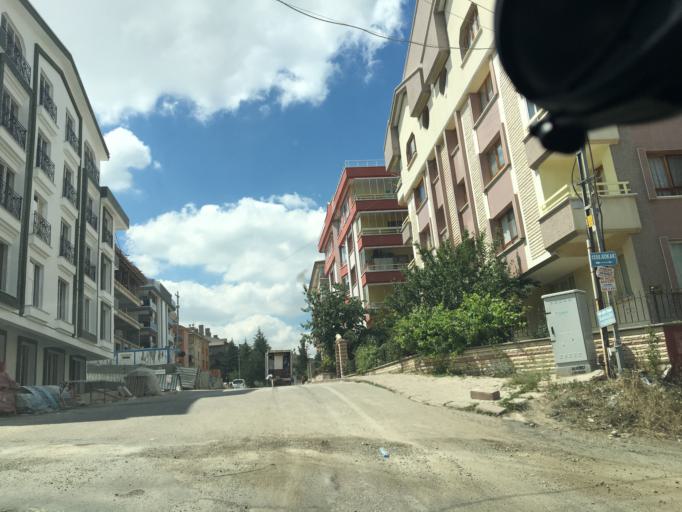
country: TR
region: Ankara
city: Ankara
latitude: 39.8831
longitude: 32.8320
